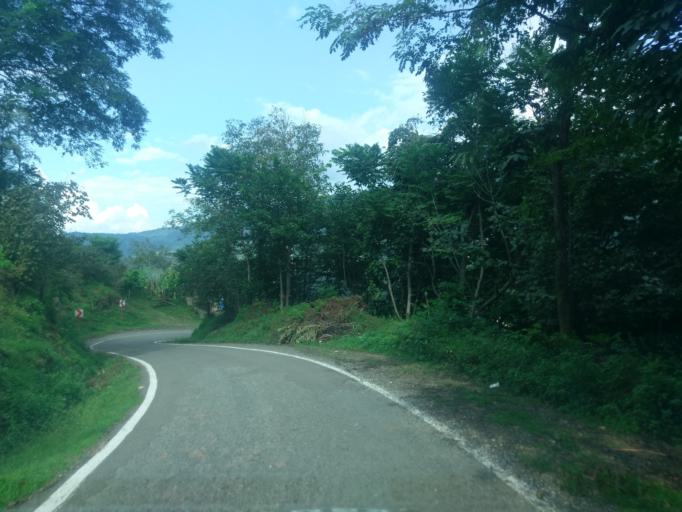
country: TR
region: Ordu
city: Camas
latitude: 40.9273
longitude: 37.6196
